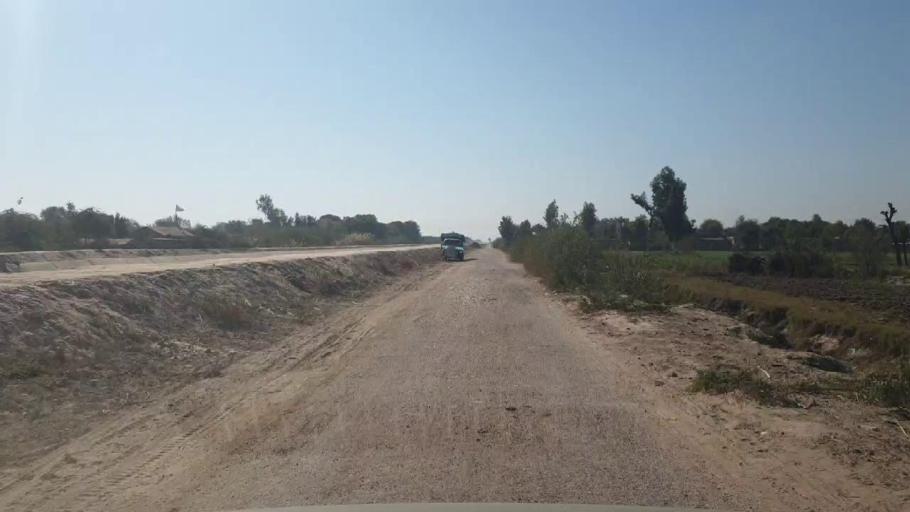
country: PK
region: Sindh
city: Mirwah Gorchani
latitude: 25.2984
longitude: 69.1030
